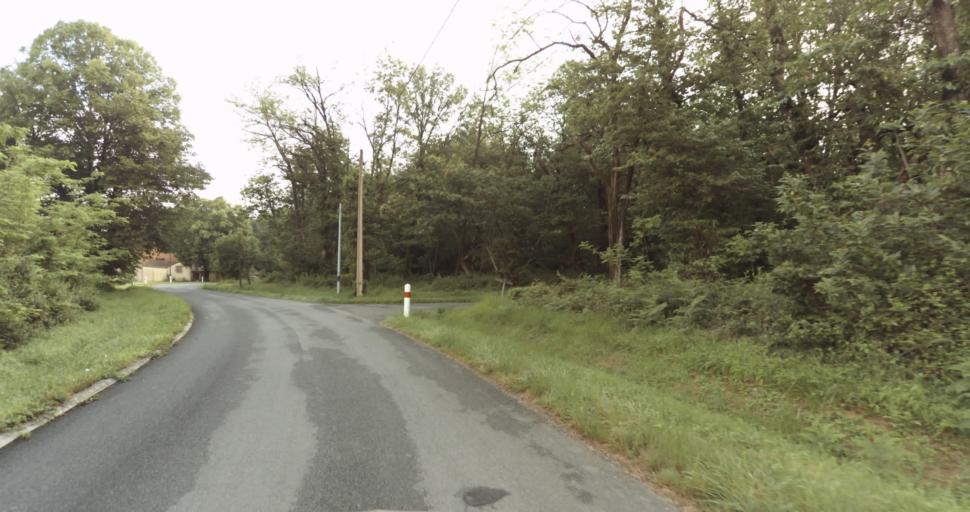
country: FR
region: Aquitaine
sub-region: Departement de la Dordogne
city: Lalinde
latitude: 44.9100
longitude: 0.7891
